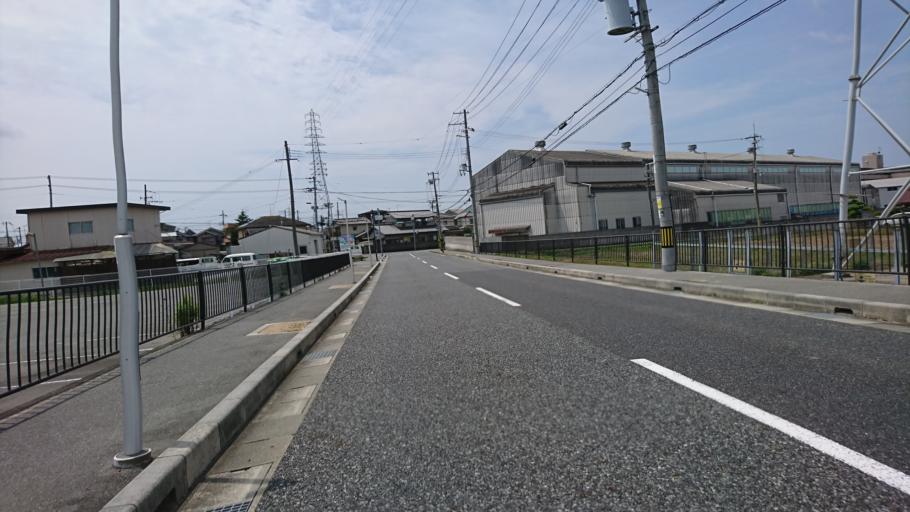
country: JP
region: Hyogo
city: Kakogawacho-honmachi
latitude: 34.7283
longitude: 134.9117
